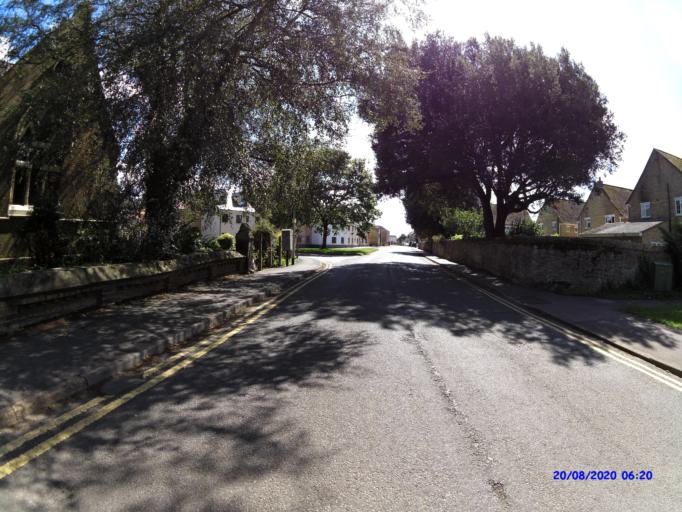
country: GB
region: England
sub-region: Cambridgeshire
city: Whittlesey
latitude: 52.5552
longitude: -0.1266
